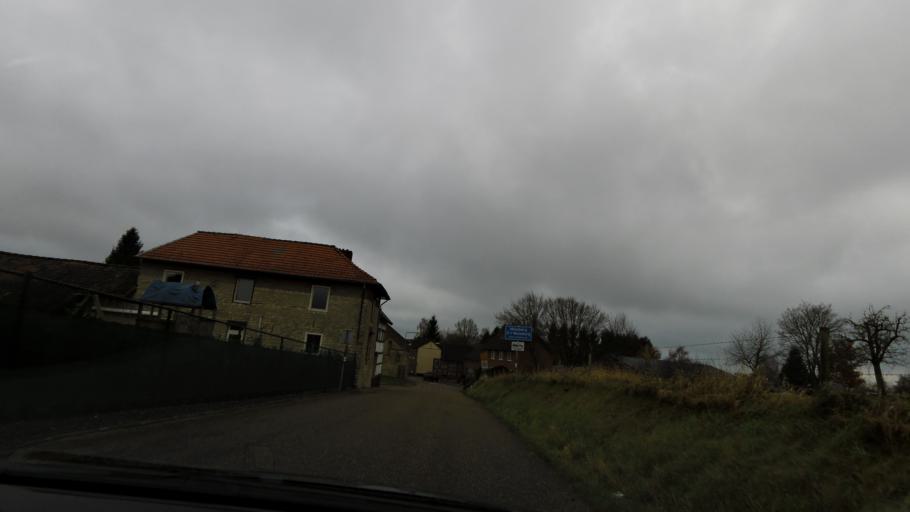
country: NL
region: Limburg
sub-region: Gemeente Simpelveld
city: Simpelveld
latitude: 50.8428
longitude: 5.9849
